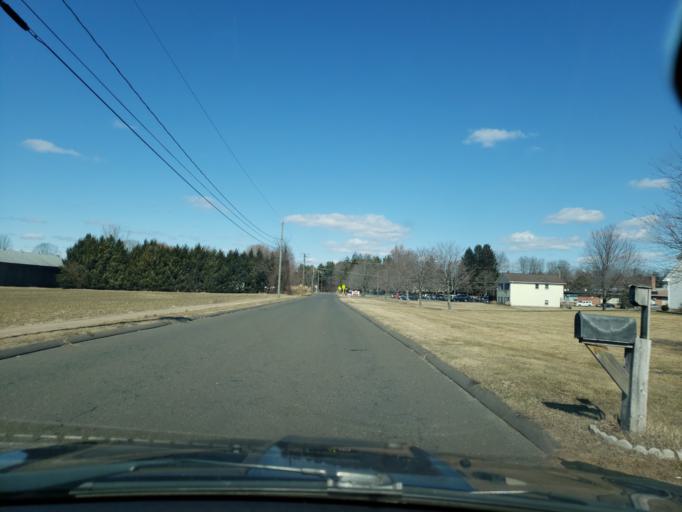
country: US
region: Connecticut
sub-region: Hartford County
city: Hazardville
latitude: 41.9826
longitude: -72.5585
